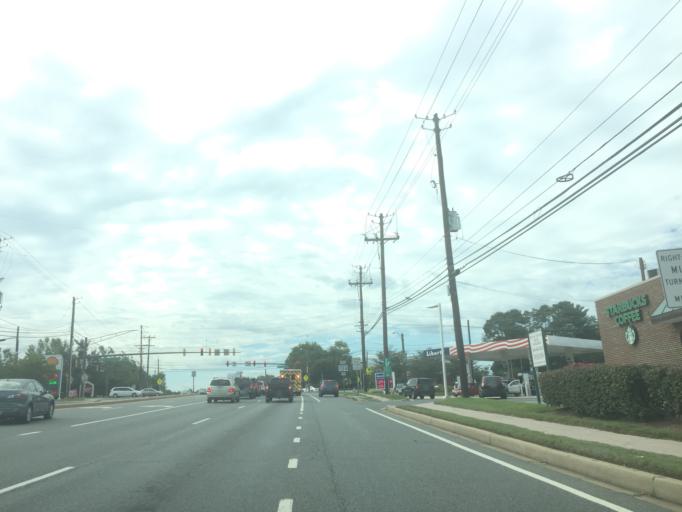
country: US
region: Maryland
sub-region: Montgomery County
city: North Potomac
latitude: 39.1176
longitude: -77.2515
